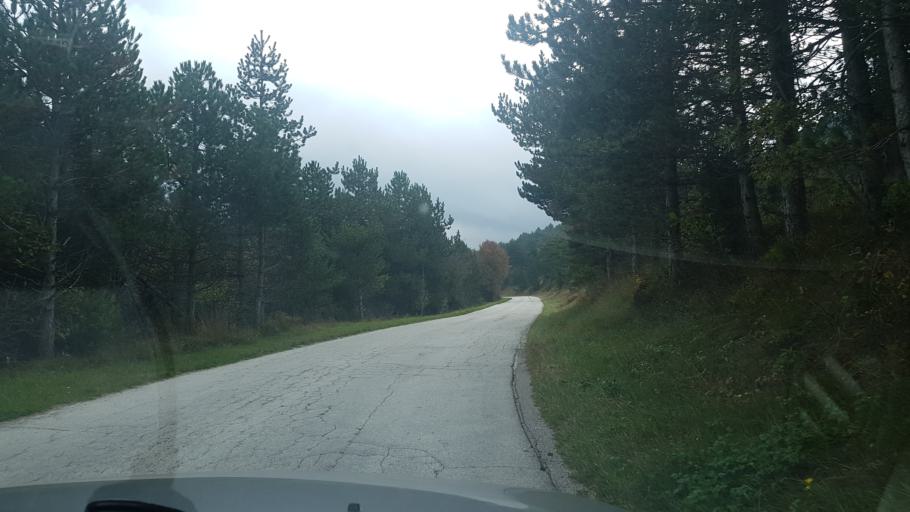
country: HR
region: Istarska
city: Buzet
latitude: 45.4958
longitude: 14.0225
